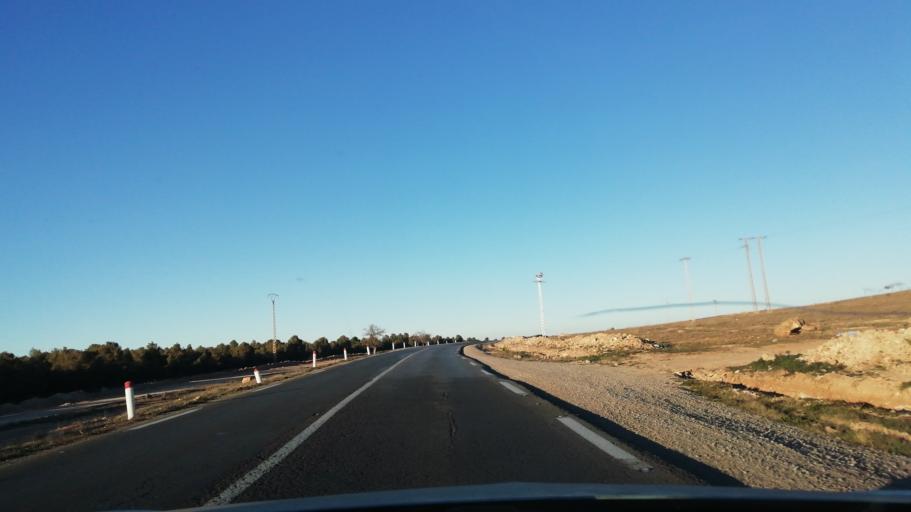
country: DZ
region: Saida
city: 'Ain el Hadjar
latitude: 34.5604
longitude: 0.1189
